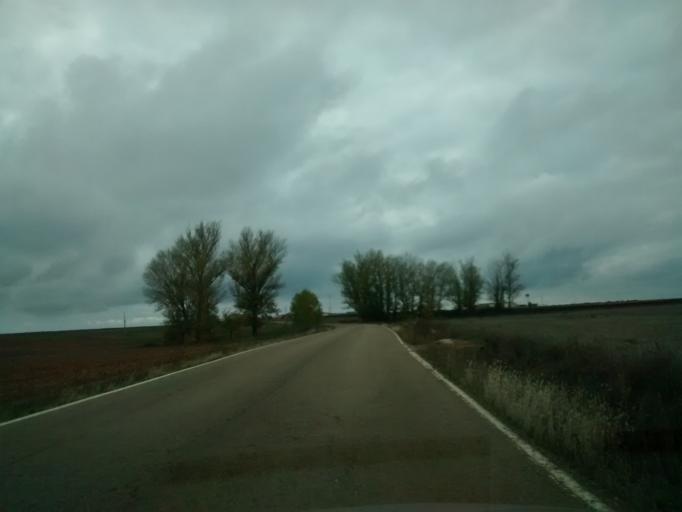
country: ES
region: Aragon
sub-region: Provincia de Zaragoza
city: Torralba de los Frailes
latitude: 41.0385
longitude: -1.6490
